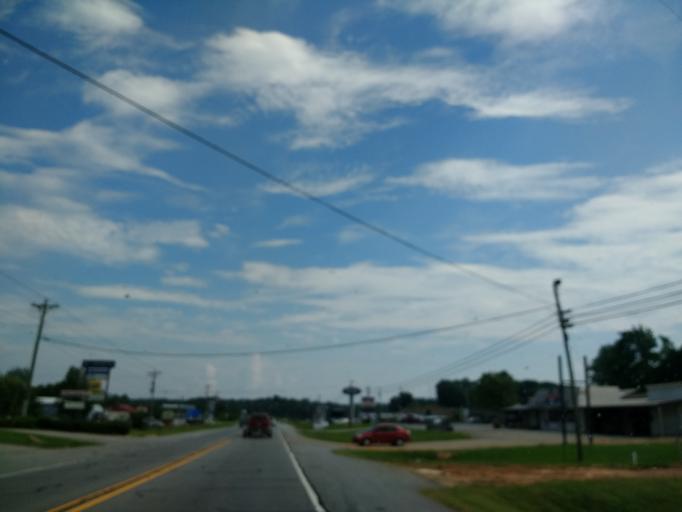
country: US
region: Georgia
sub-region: White County
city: Cleveland
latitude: 34.5598
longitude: -83.7626
